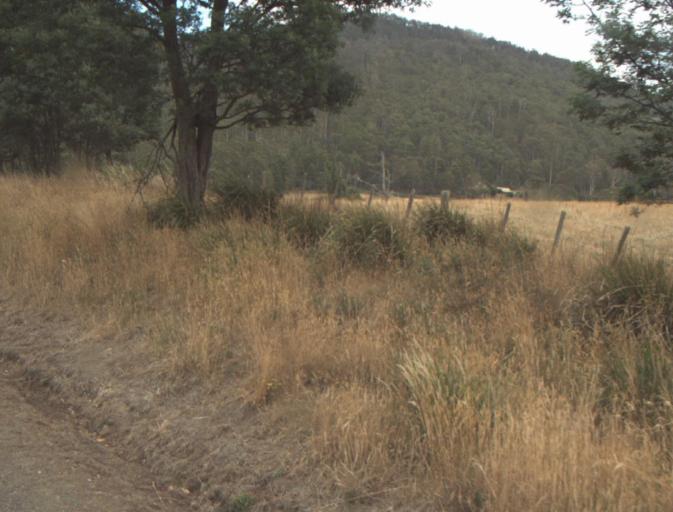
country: AU
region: Tasmania
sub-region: Northern Midlands
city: Evandale
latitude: -41.4615
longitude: 147.4546
